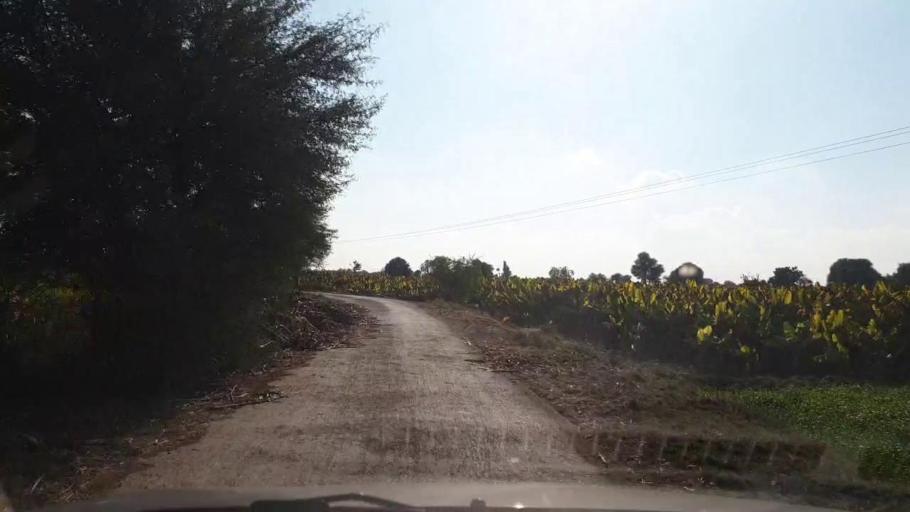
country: PK
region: Sindh
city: Sinjhoro
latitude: 25.9914
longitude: 68.7272
